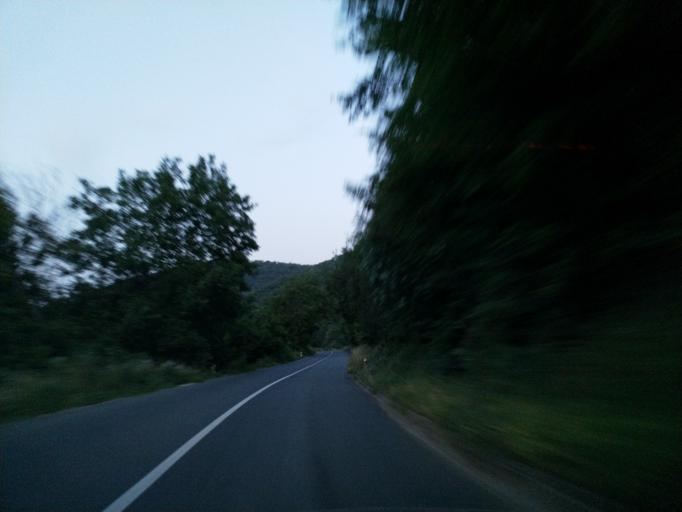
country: RS
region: Central Serbia
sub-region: Rasinski Okrug
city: Aleksandrovac
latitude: 43.3438
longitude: 21.1081
